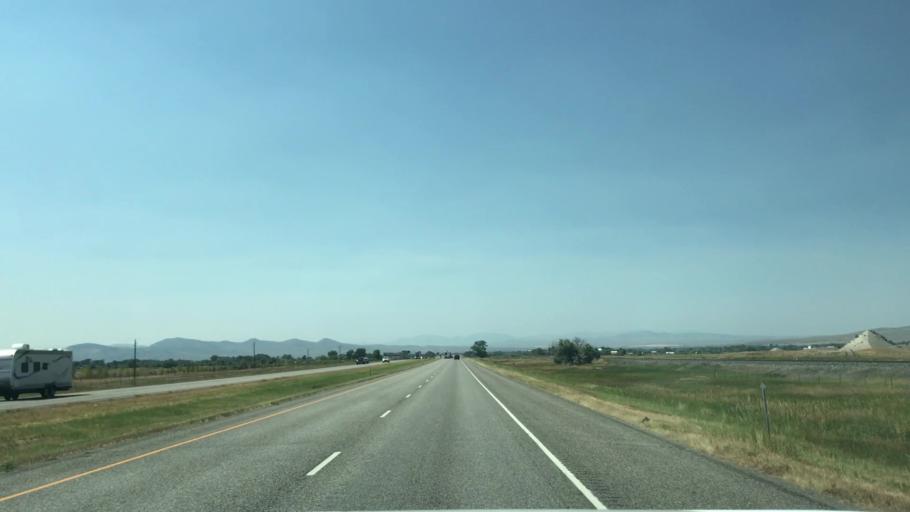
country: US
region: Montana
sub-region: Gallatin County
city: Three Forks
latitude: 45.8918
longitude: -111.4736
